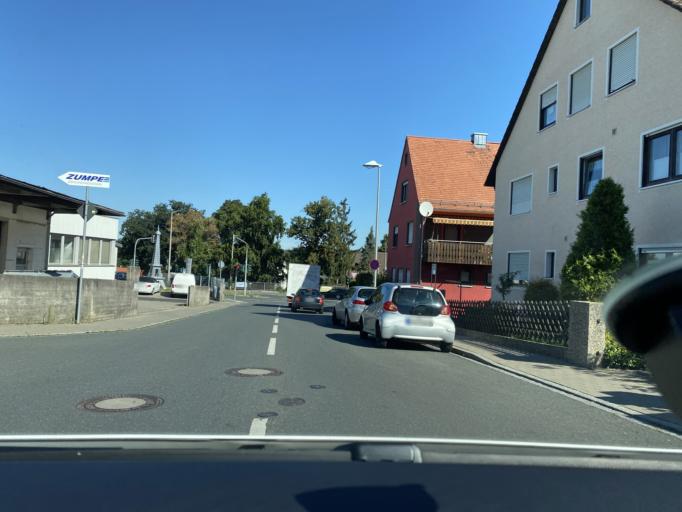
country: DE
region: Bavaria
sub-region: Regierungsbezirk Mittelfranken
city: Zirndorf
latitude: 49.4334
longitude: 10.9563
